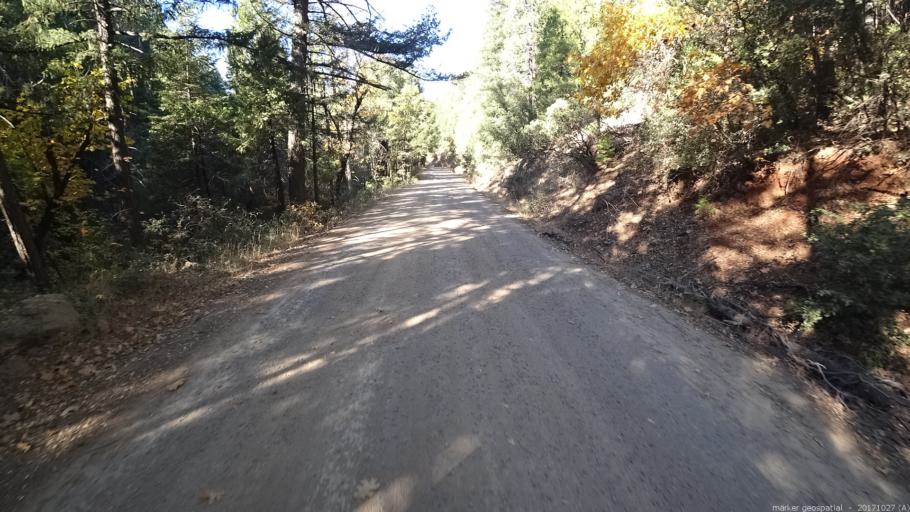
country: US
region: California
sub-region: Shasta County
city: Bella Vista
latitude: 40.8152
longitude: -121.9849
